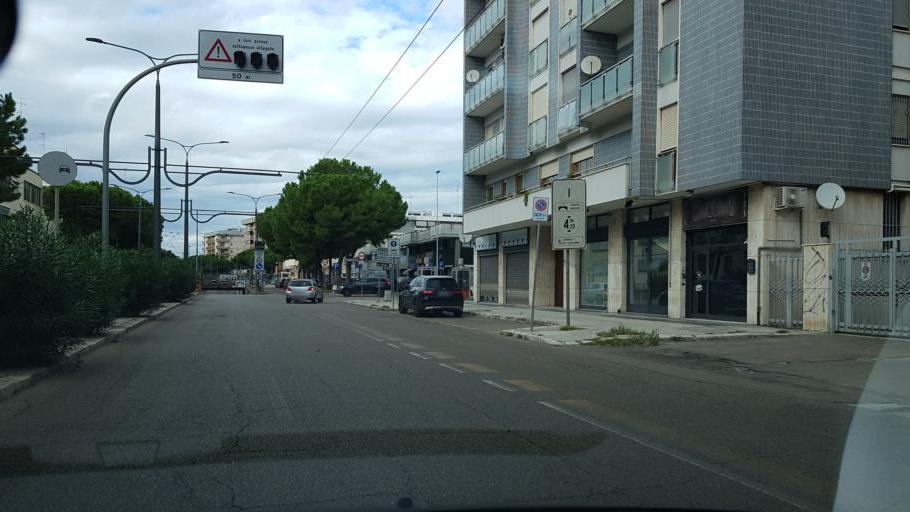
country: IT
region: Apulia
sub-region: Provincia di Lecce
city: Lecce
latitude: 40.3555
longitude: 18.1851
